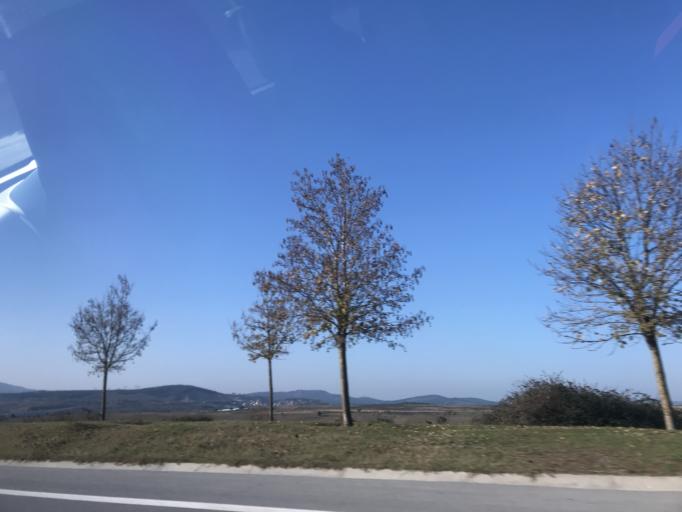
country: TR
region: Kocaeli
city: Balcik
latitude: 40.9418
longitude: 29.3713
